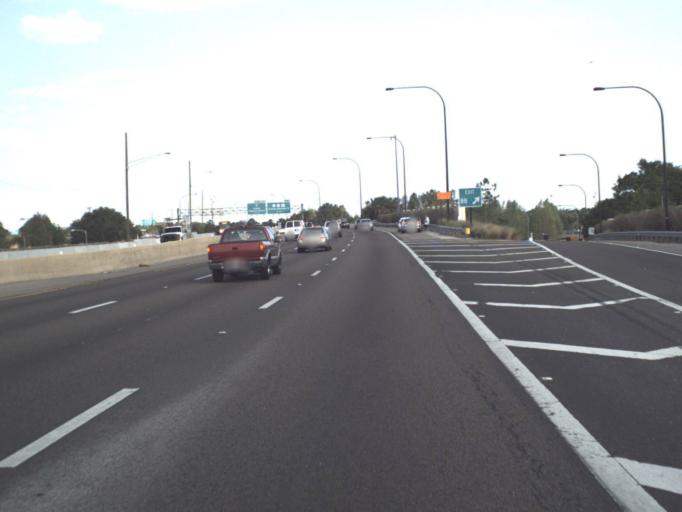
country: US
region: Florida
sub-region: Orange County
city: Orlando
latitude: 28.5375
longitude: -81.4073
